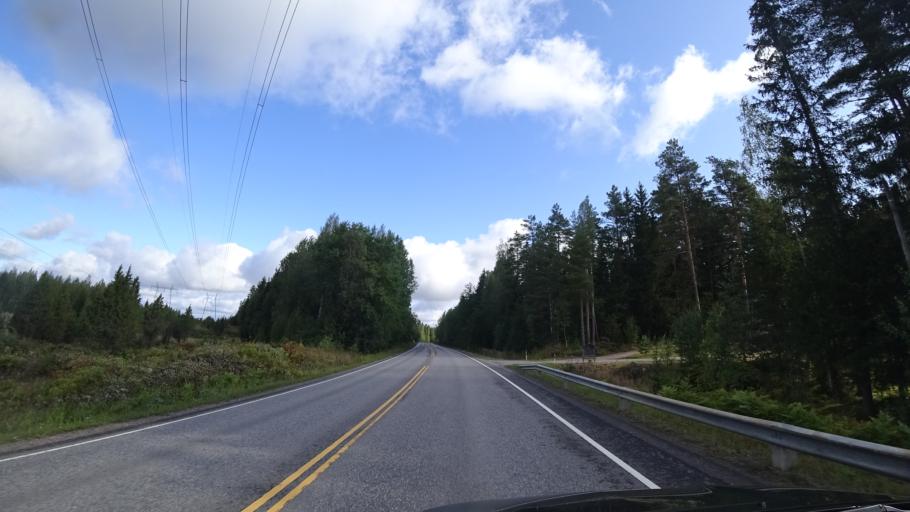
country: FI
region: Uusimaa
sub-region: Helsinki
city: Hyvinge
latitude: 60.5357
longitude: 24.9224
